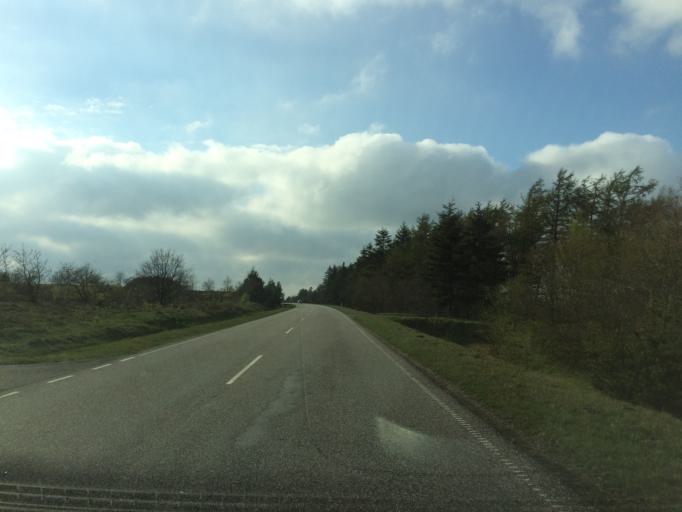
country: DK
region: Central Jutland
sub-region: Viborg Kommune
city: Karup
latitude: 56.3353
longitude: 9.0926
